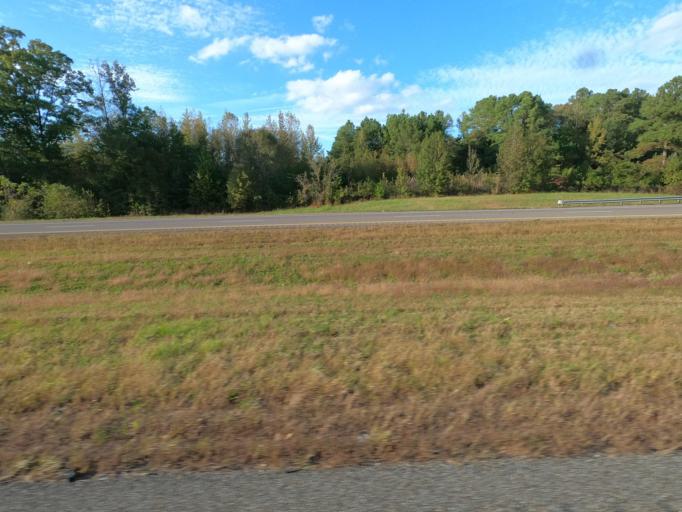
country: US
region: Tennessee
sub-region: Henderson County
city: Lexington
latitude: 35.7588
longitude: -88.4942
